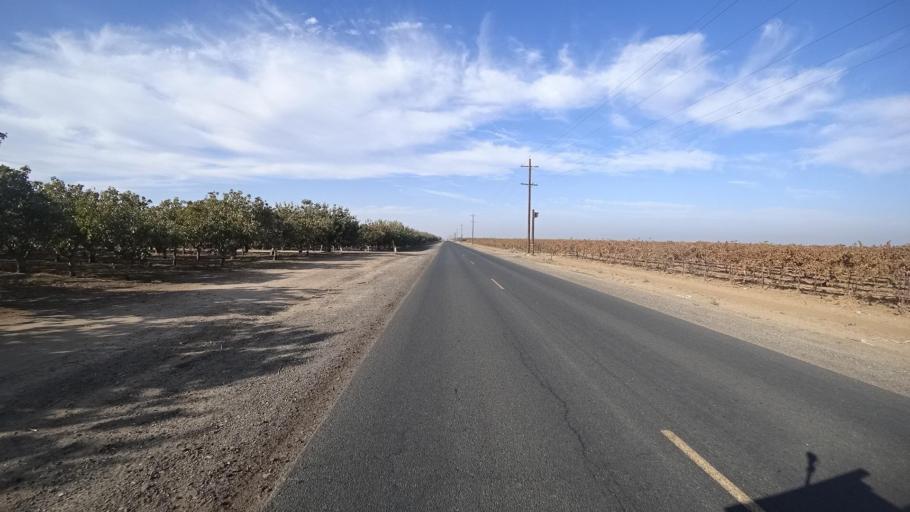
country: US
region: California
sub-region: Kern County
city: McFarland
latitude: 35.6021
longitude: -119.1594
